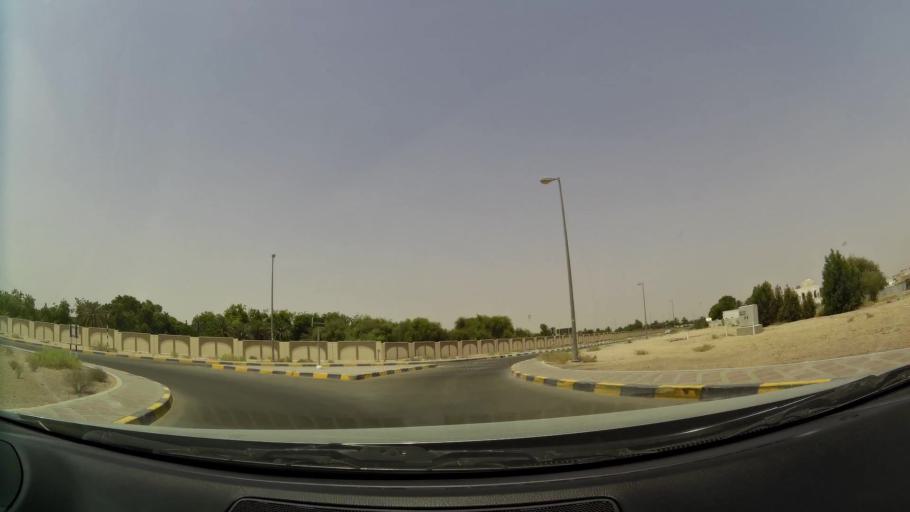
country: AE
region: Abu Dhabi
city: Al Ain
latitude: 24.1864
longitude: 55.7362
